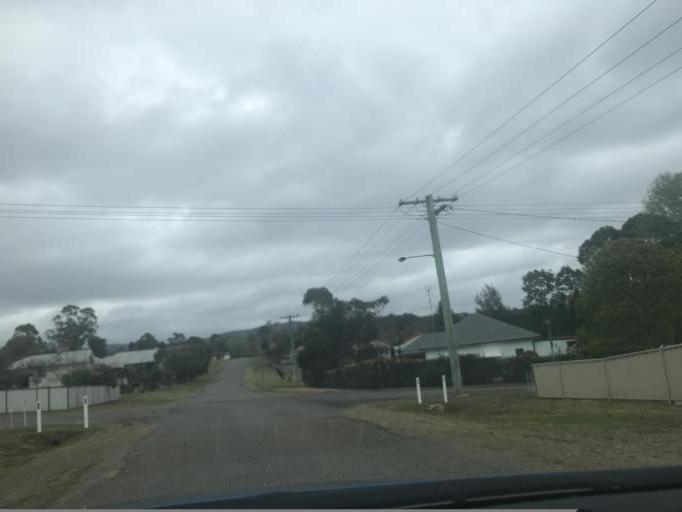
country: AU
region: New South Wales
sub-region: Cessnock
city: Cessnock
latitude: -32.9042
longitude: 151.2876
